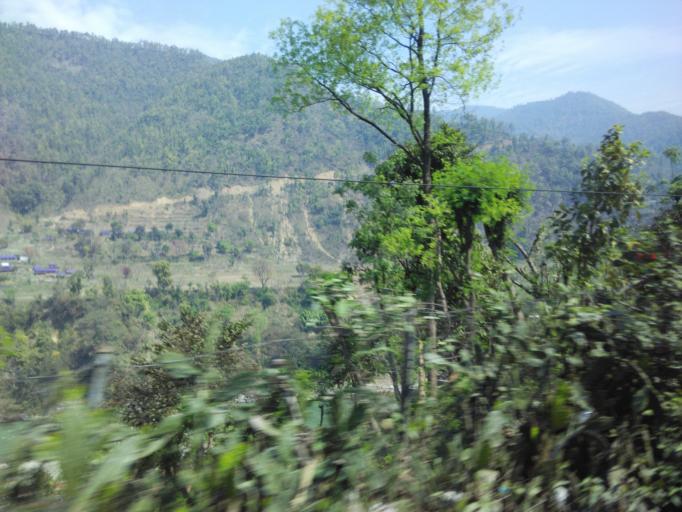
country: NP
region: Central Region
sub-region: Narayani Zone
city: Bharatpur
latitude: 27.8775
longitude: 84.5907
